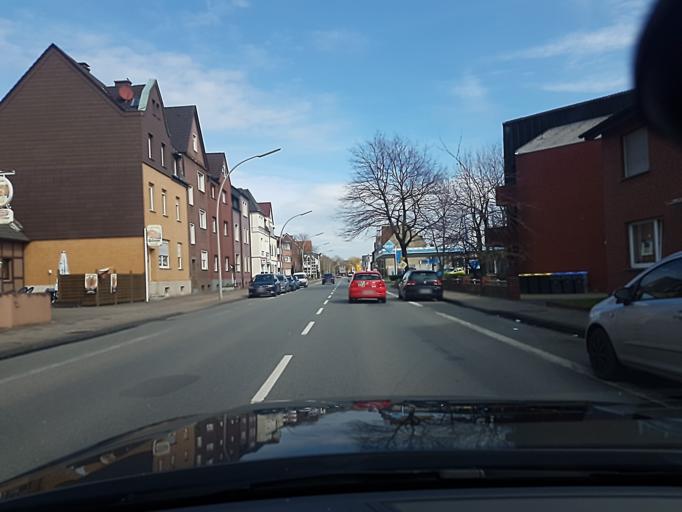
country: DE
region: North Rhine-Westphalia
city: Werne
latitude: 51.6570
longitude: 7.6279
